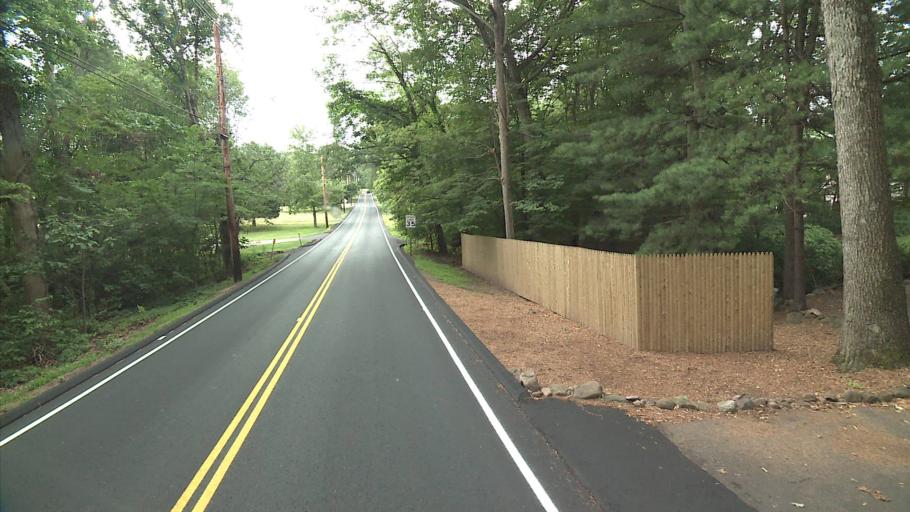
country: US
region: Connecticut
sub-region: New Haven County
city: Wallingford Center
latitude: 41.4027
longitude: -72.8014
